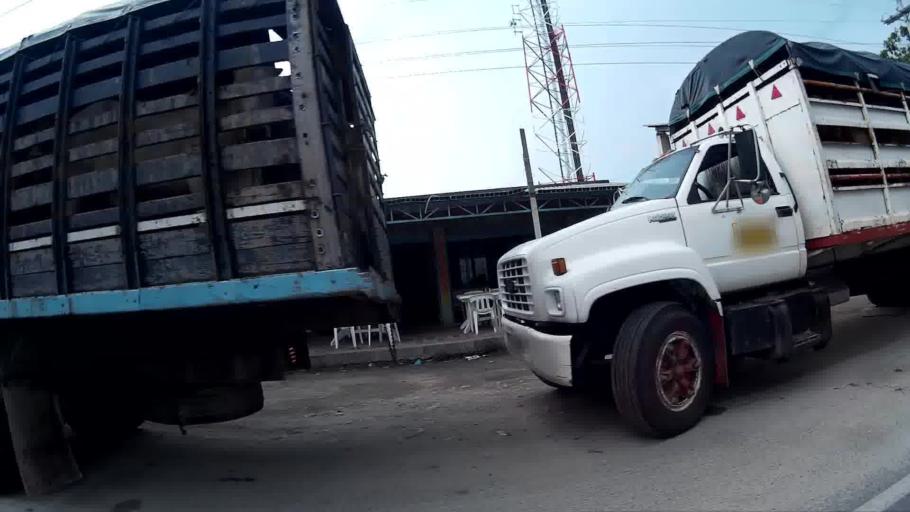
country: CO
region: Magdalena
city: Cienaga
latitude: 11.0043
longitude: -74.2293
